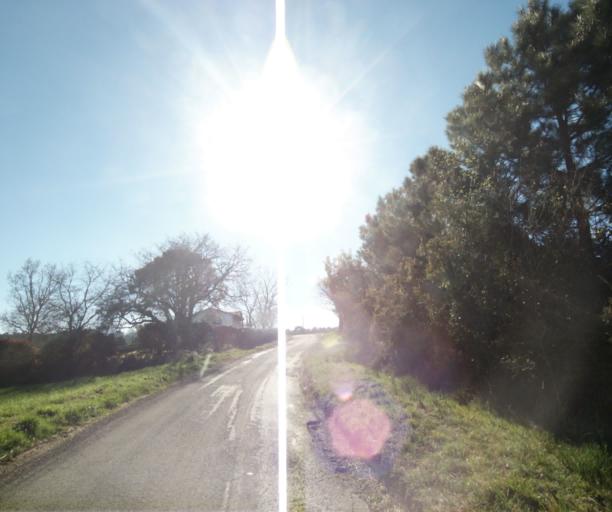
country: FR
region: Aquitaine
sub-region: Departement des Pyrenees-Atlantiques
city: Hendaye
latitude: 43.3607
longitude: -1.7380
